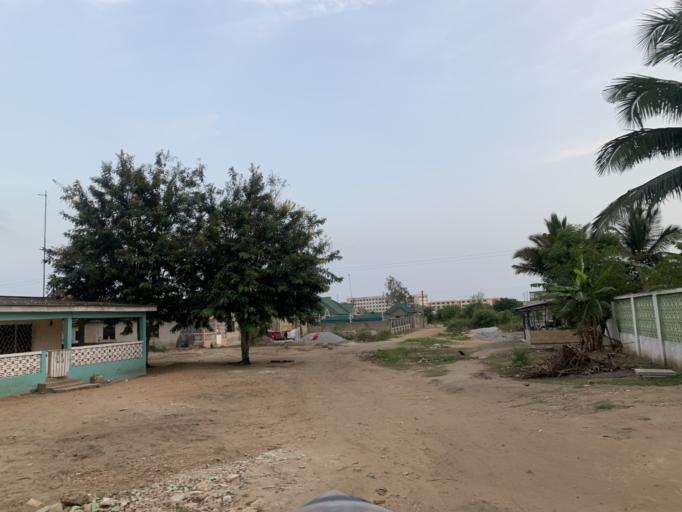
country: GH
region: Central
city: Winneba
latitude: 5.3758
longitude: -0.6321
